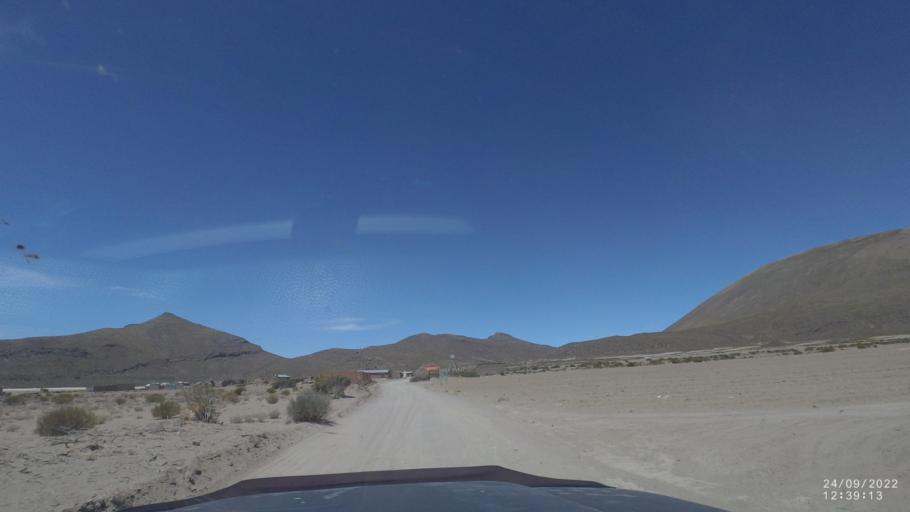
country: BO
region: Potosi
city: Colchani
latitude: -19.7932
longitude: -67.5800
